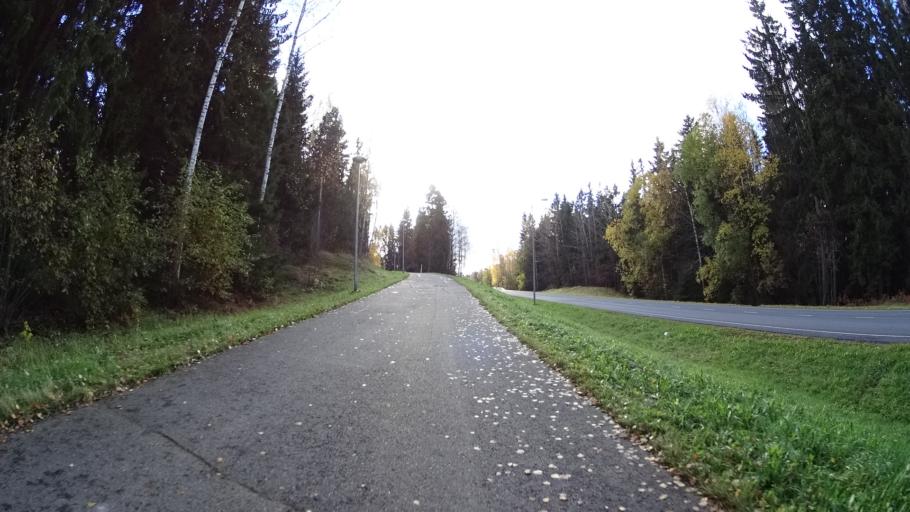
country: FI
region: Uusimaa
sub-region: Helsinki
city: Kilo
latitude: 60.2799
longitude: 24.8366
